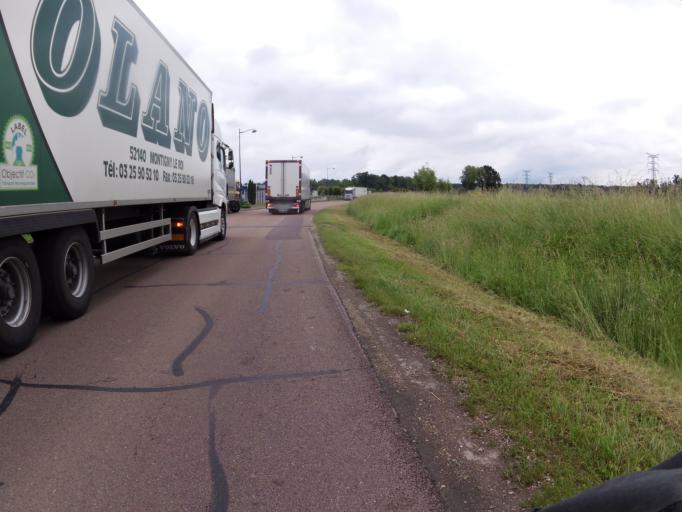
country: FR
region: Champagne-Ardenne
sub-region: Departement de la Haute-Marne
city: Saint-Dizier
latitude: 48.6518
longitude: 4.9346
